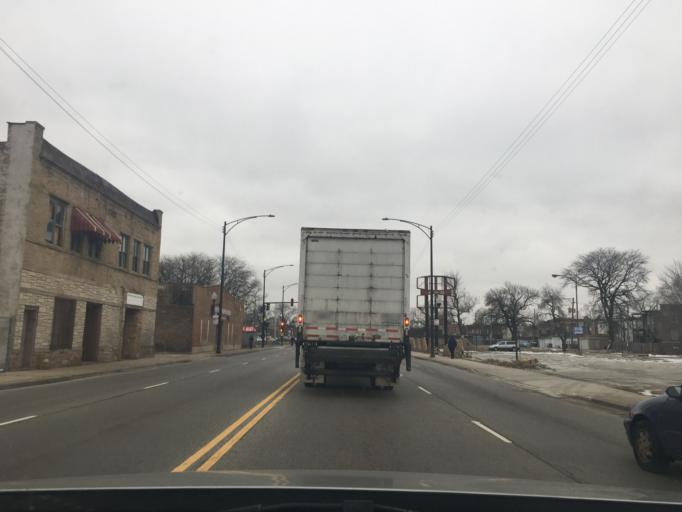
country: US
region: Illinois
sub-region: Cook County
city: Oak Park
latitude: 41.8853
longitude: -87.7455
